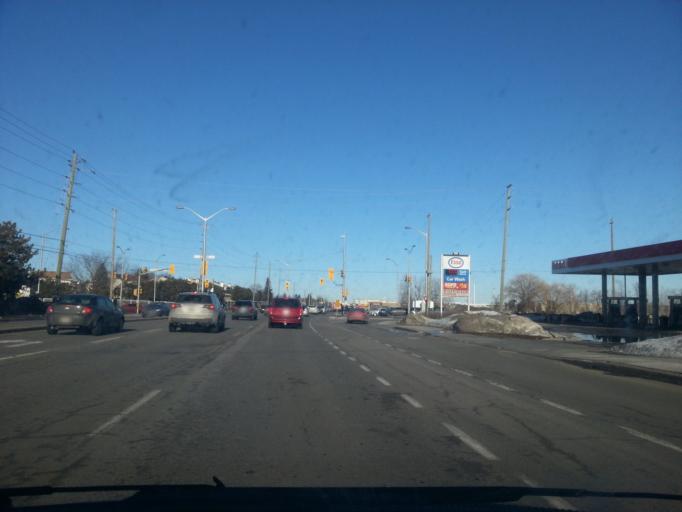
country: CA
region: Quebec
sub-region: Outaouais
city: Gatineau
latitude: 45.4556
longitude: -75.5062
